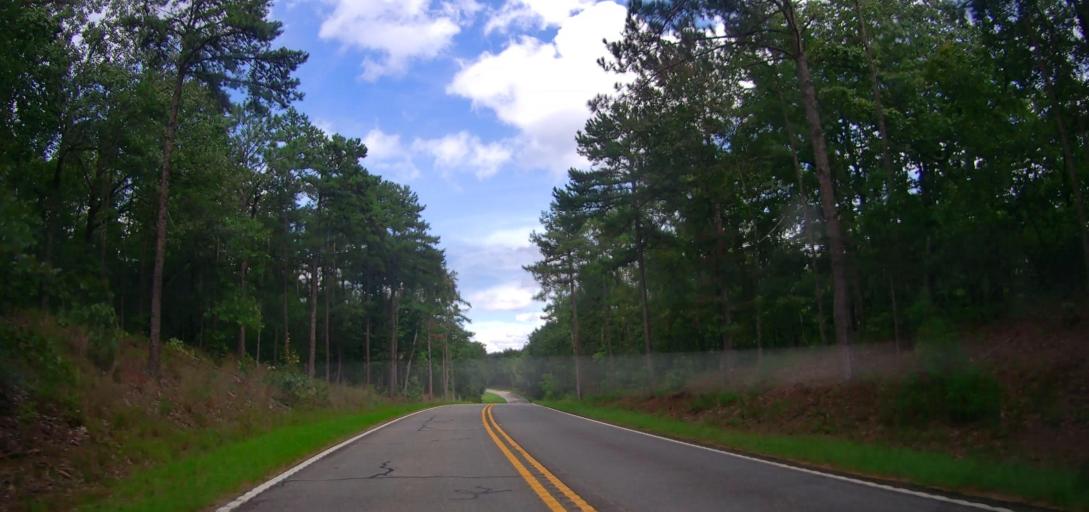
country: US
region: Georgia
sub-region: Meriwether County
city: Manchester
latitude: 32.8633
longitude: -84.7290
